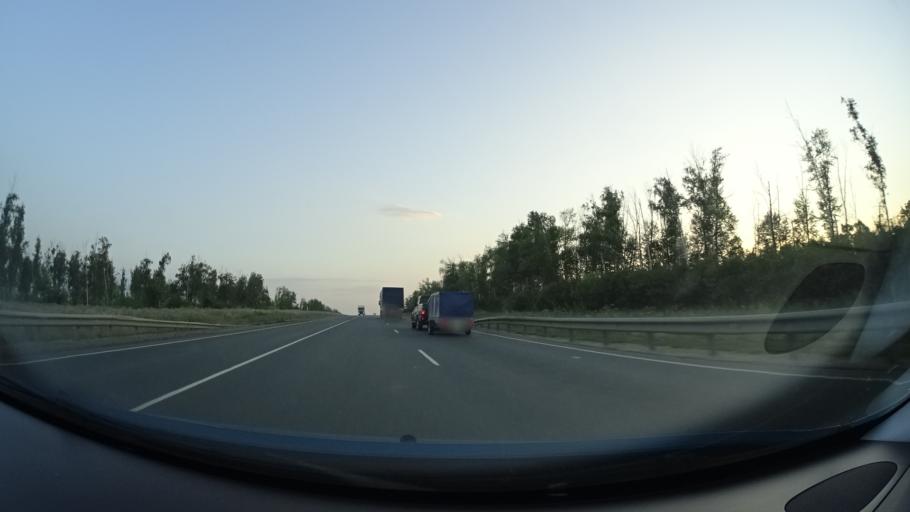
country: RU
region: Samara
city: Sukhodol
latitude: 53.8341
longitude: 51.0902
